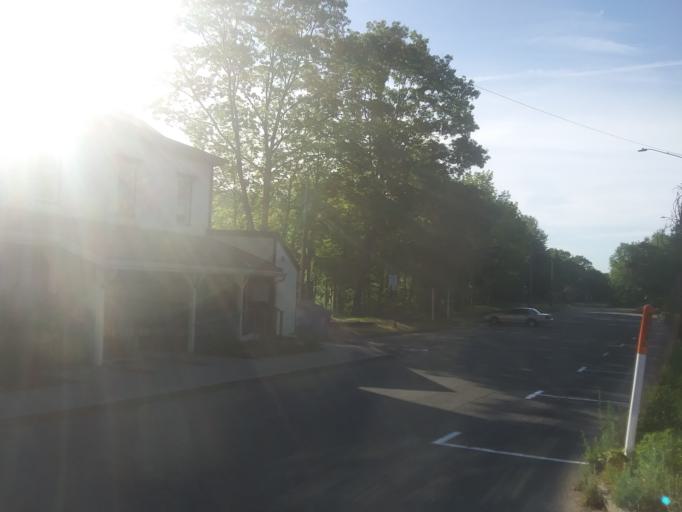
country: US
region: Massachusetts
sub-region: Franklin County
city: Shelburne Falls
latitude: 42.6020
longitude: -72.7418
